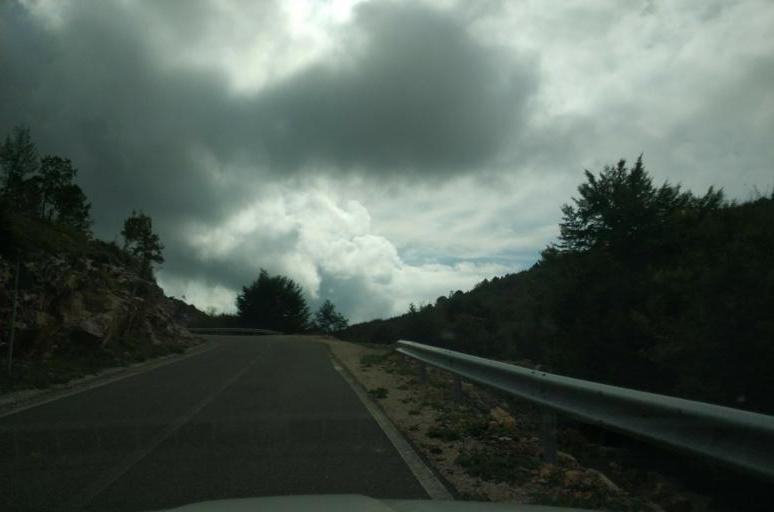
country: AL
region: Durres
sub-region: Rrethi i Krujes
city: Kruje
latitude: 41.5210
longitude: 19.8050
